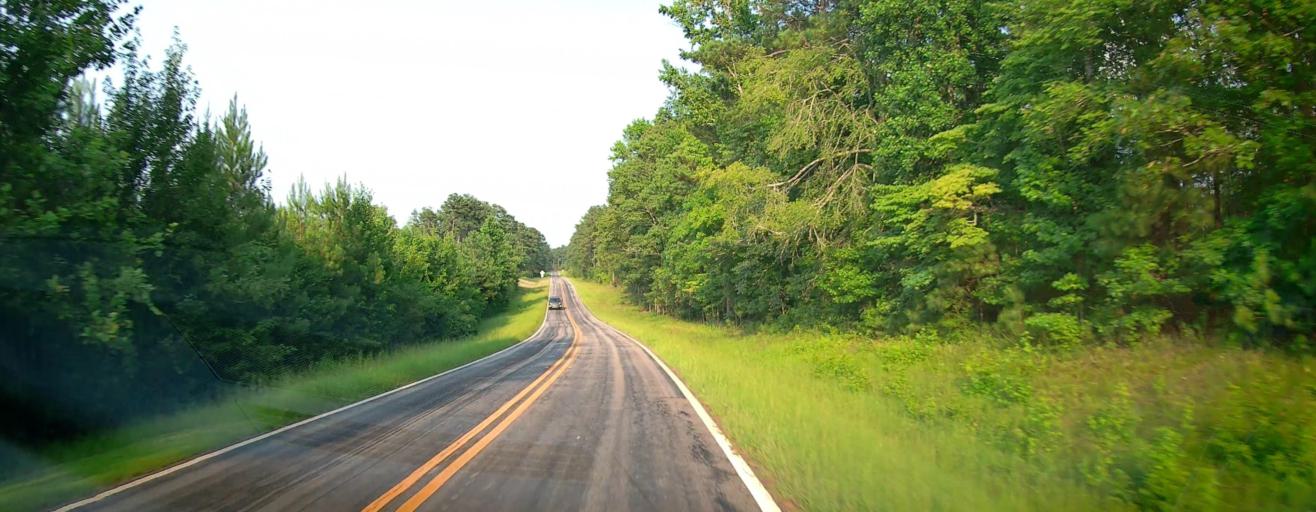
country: US
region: Georgia
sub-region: Jones County
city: Gray
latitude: 33.1122
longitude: -83.6471
